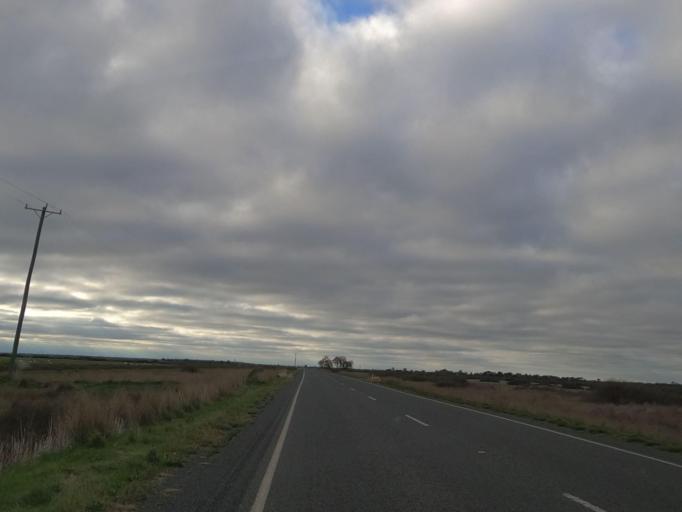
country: AU
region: Victoria
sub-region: Swan Hill
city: Swan Hill
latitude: -35.8527
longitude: 143.9367
